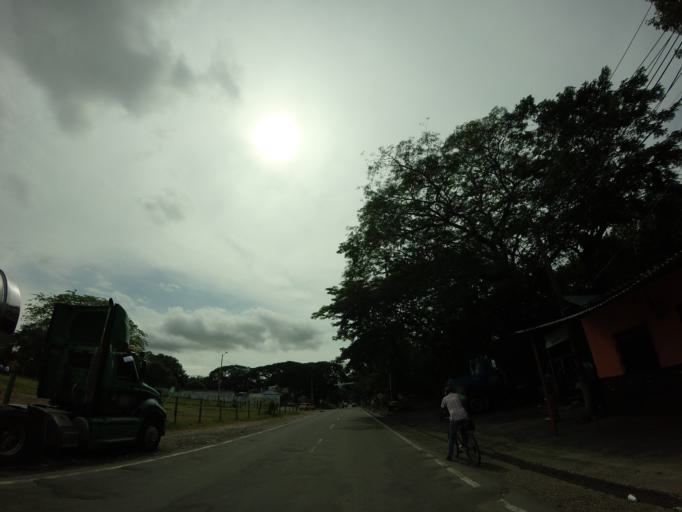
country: CO
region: Caldas
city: La Dorada
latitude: 5.4463
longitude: -74.6722
